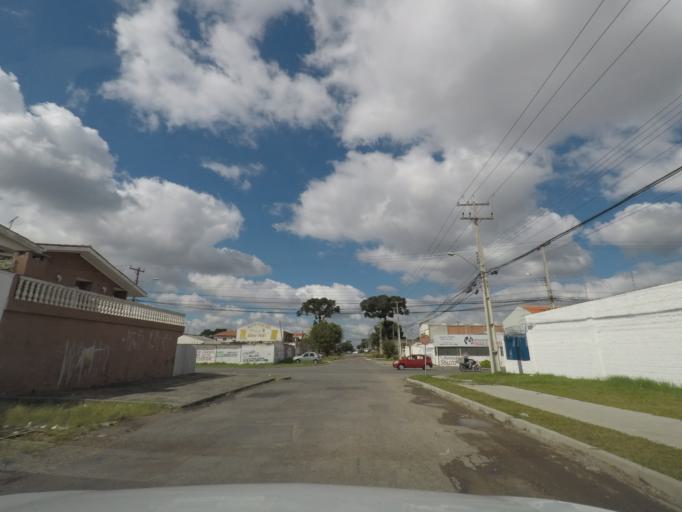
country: BR
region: Parana
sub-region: Sao Jose Dos Pinhais
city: Sao Jose dos Pinhais
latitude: -25.5021
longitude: -49.2244
